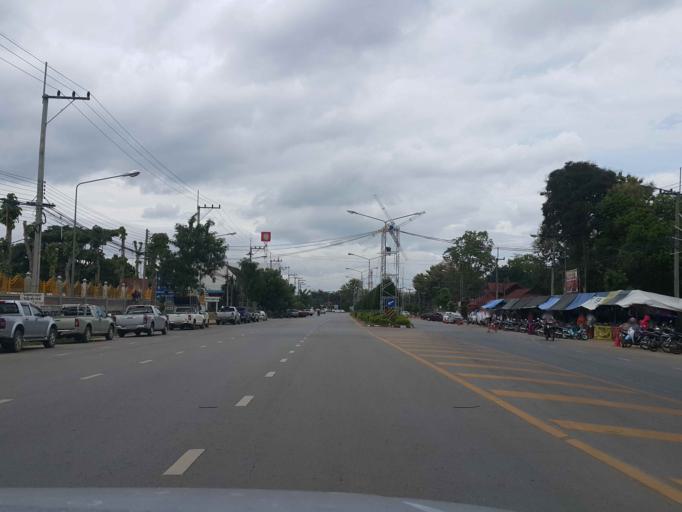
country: TH
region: Lamphun
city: Li
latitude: 17.7998
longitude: 98.9504
